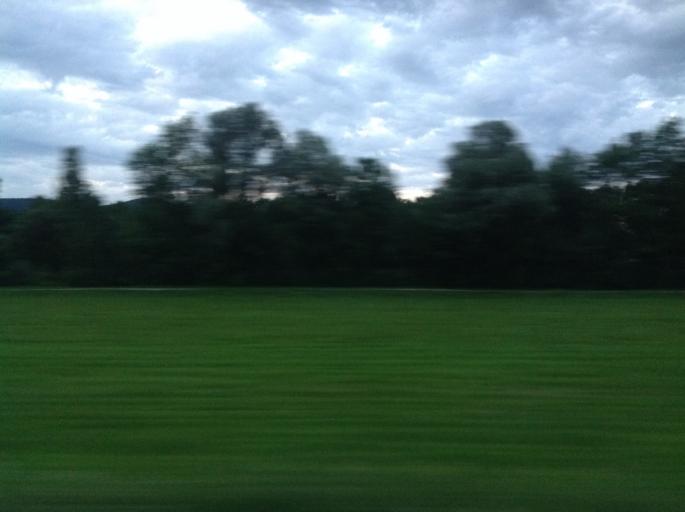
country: DE
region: Bavaria
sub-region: Upper Bavaria
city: Piding
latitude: 47.7710
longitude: 12.8932
